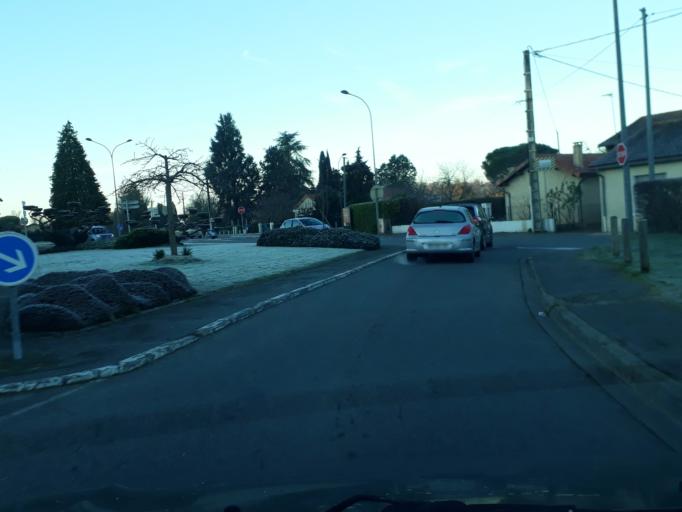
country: FR
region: Midi-Pyrenees
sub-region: Departement du Gers
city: Auch
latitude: 43.6302
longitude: 0.5875
